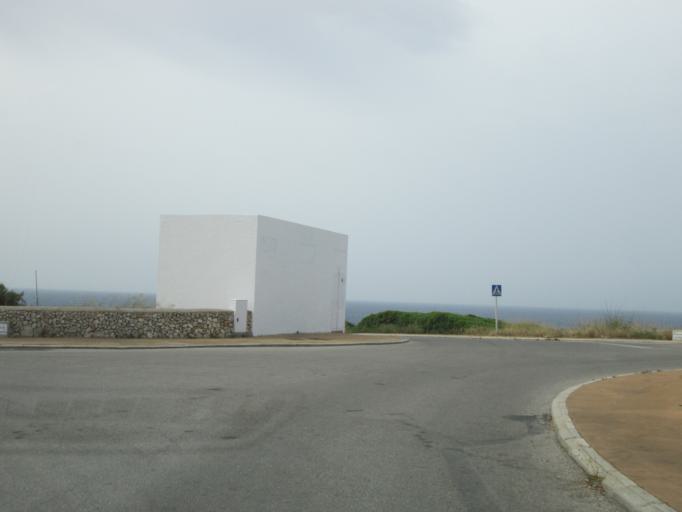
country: ES
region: Balearic Islands
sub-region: Illes Balears
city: Sant Lluis
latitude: 39.8355
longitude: 4.1934
